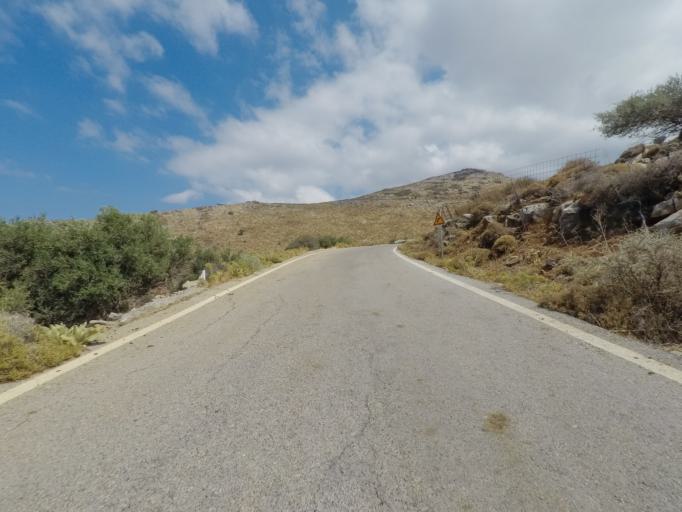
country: GR
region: Crete
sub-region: Nomos Lasithiou
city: Elounda
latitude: 35.3146
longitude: 25.6769
